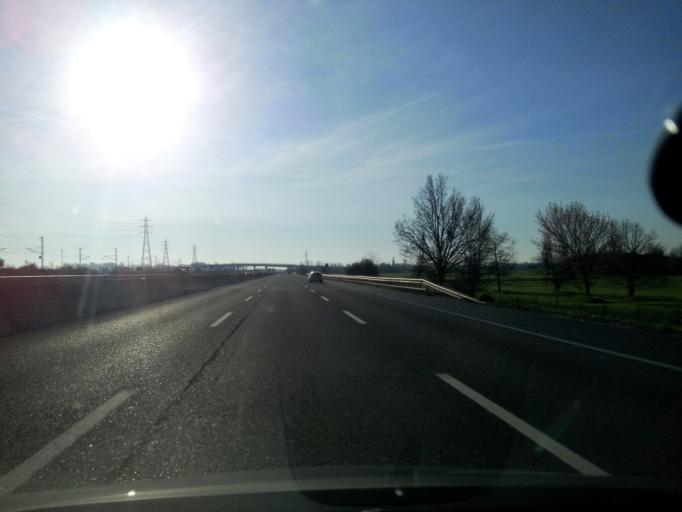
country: IT
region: Emilia-Romagna
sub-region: Provincia di Parma
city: San Prospero
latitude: 44.8122
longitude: 10.4181
